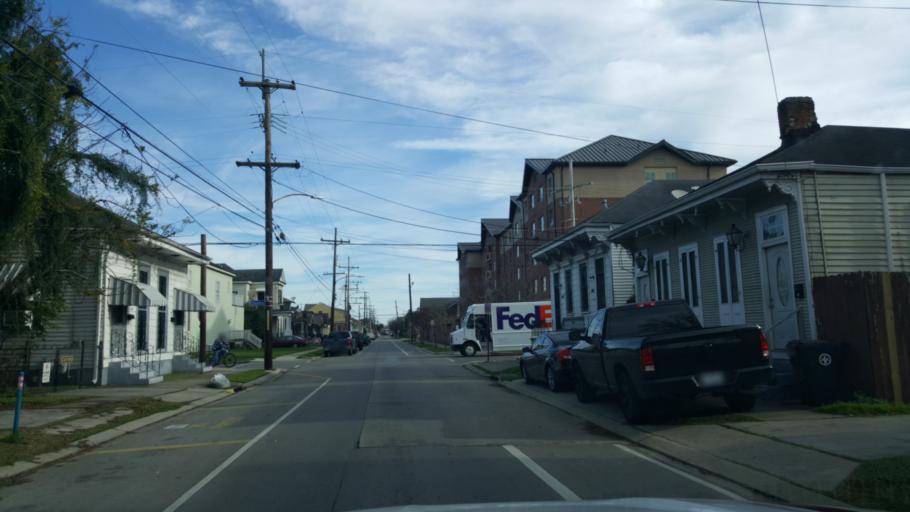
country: US
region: Louisiana
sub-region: Orleans Parish
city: New Orleans
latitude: 29.9737
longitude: -90.0719
